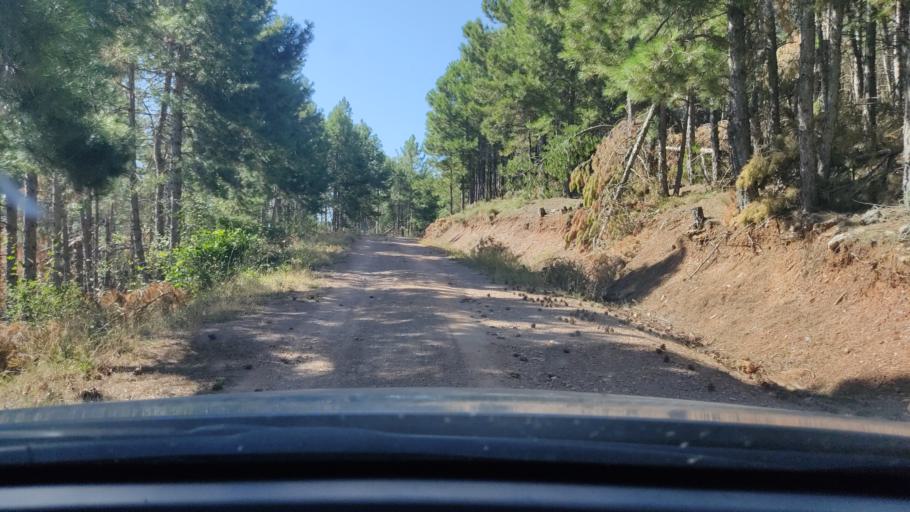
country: ES
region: Aragon
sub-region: Provincia de Teruel
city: Monforte de Moyuela
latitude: 41.0317
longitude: -1.0477
